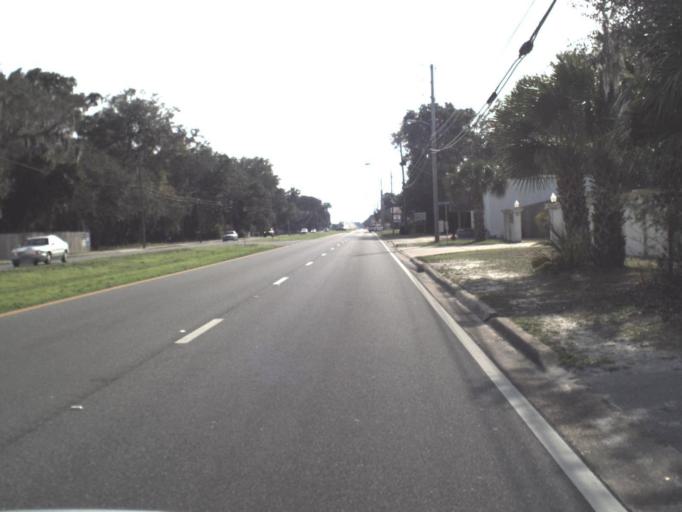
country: US
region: Florida
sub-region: Bay County
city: Parker
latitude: 30.1174
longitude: -85.5968
